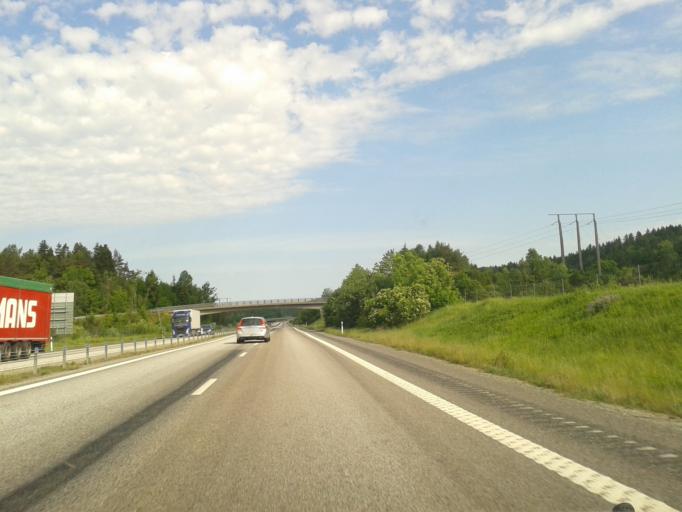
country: SE
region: Vaestra Goetaland
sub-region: Munkedals Kommun
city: Munkedal
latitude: 58.5299
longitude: 11.5401
